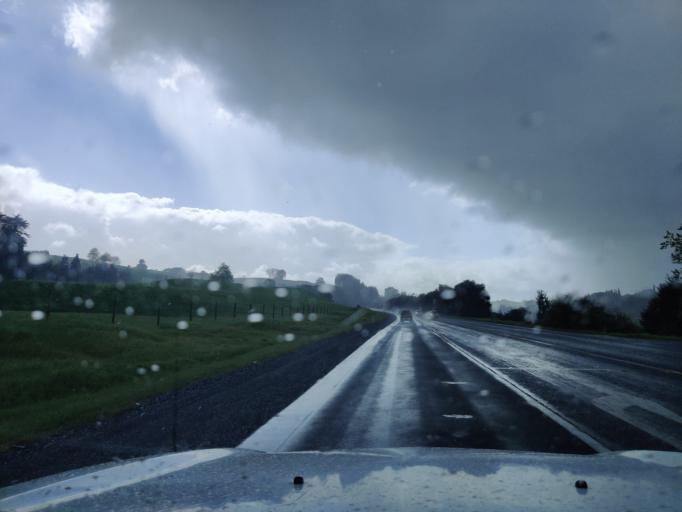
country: NZ
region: Waikato
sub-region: Waipa District
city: Cambridge
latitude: -37.9467
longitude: 175.5942
